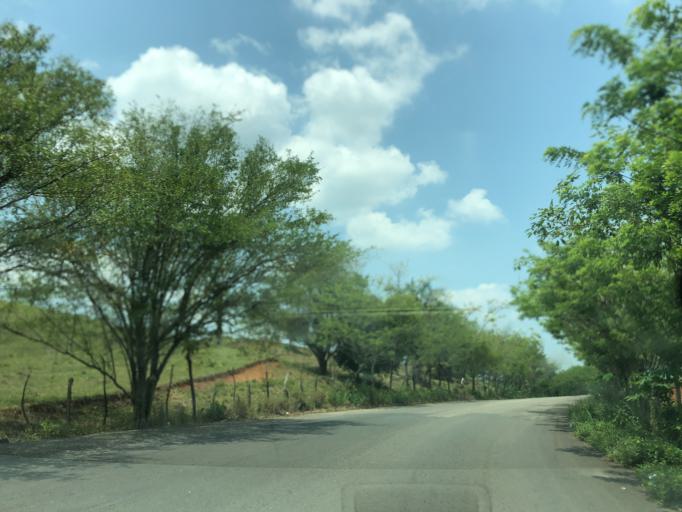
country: MX
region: Chiapas
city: Pueblo Juarez
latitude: 17.7266
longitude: -93.1710
